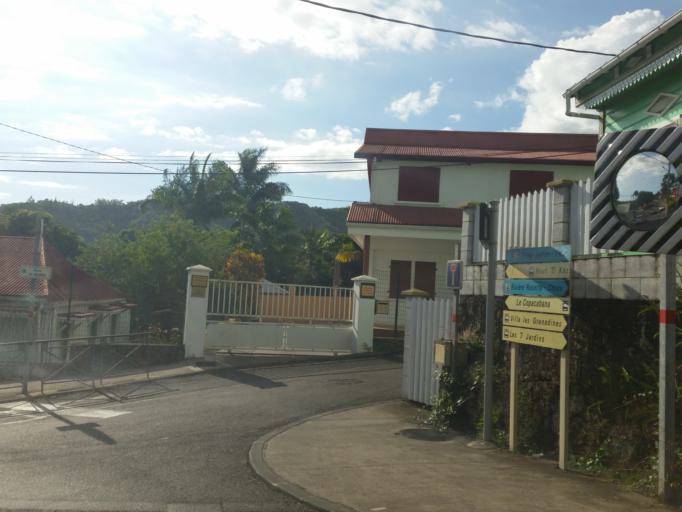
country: RE
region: Reunion
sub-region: Reunion
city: L'Entre-Deux
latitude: -21.2472
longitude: 55.4728
